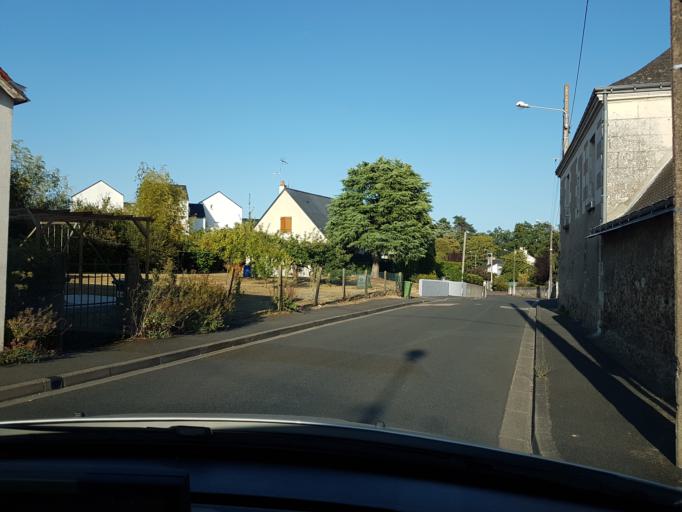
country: FR
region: Centre
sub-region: Departement d'Indre-et-Loire
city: Saint-Avertin
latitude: 47.3591
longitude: 0.7277
